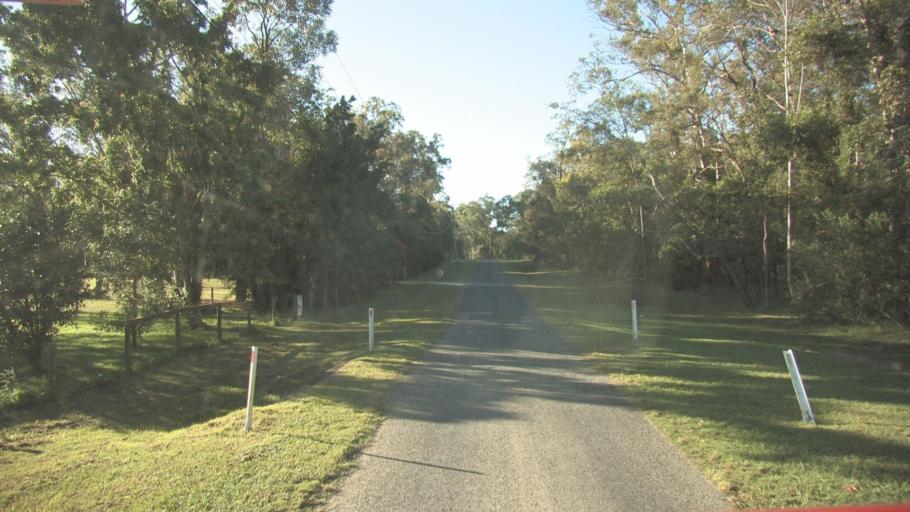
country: AU
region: Queensland
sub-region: Gold Coast
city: Yatala
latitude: -27.6638
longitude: 153.2453
